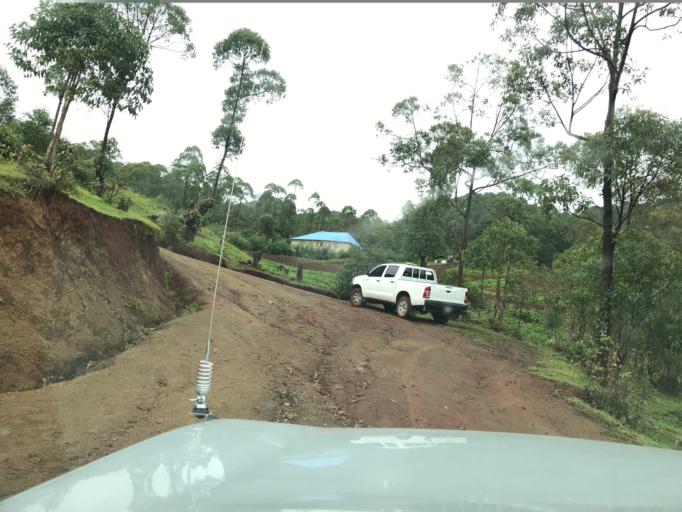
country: TL
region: Ainaro
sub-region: Ainaro
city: Ainaro
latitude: -8.8744
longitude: 125.5508
